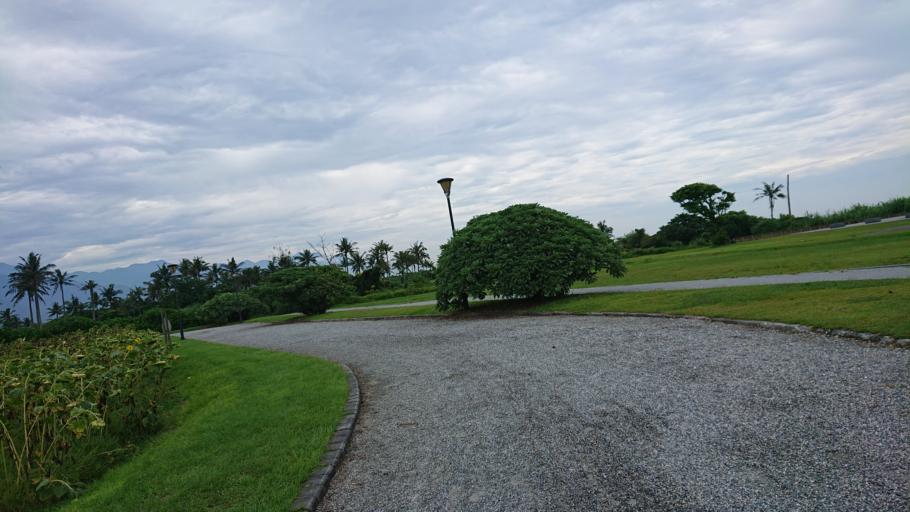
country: TW
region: Taiwan
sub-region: Hualien
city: Hualian
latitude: 23.9388
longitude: 121.6027
